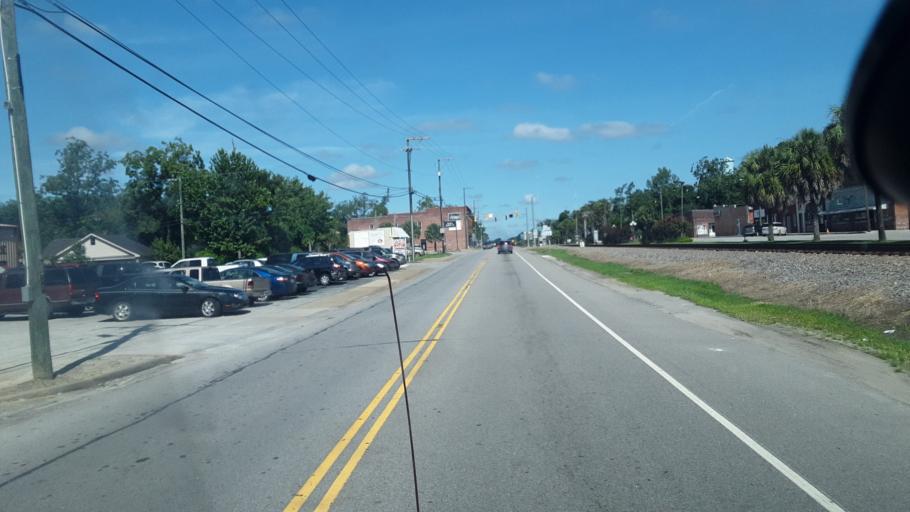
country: US
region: South Carolina
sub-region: Hampton County
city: Varnville
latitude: 32.8494
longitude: -81.0791
